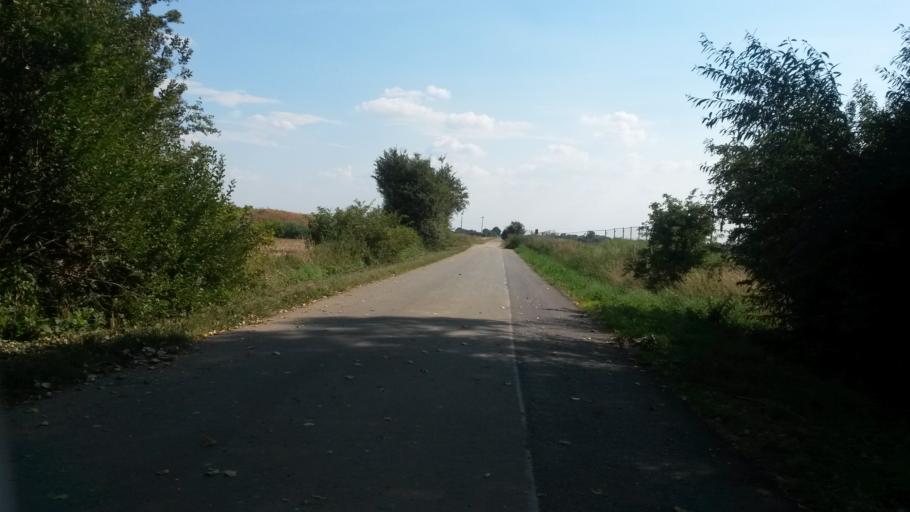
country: DE
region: Lower Saxony
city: Riede
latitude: 53.0277
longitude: 8.9115
